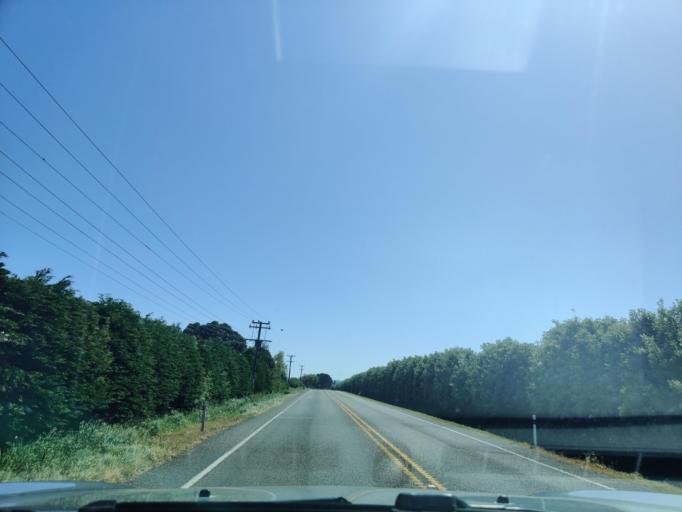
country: NZ
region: Taranaki
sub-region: South Taranaki District
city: Hawera
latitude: -39.6559
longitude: 174.3942
